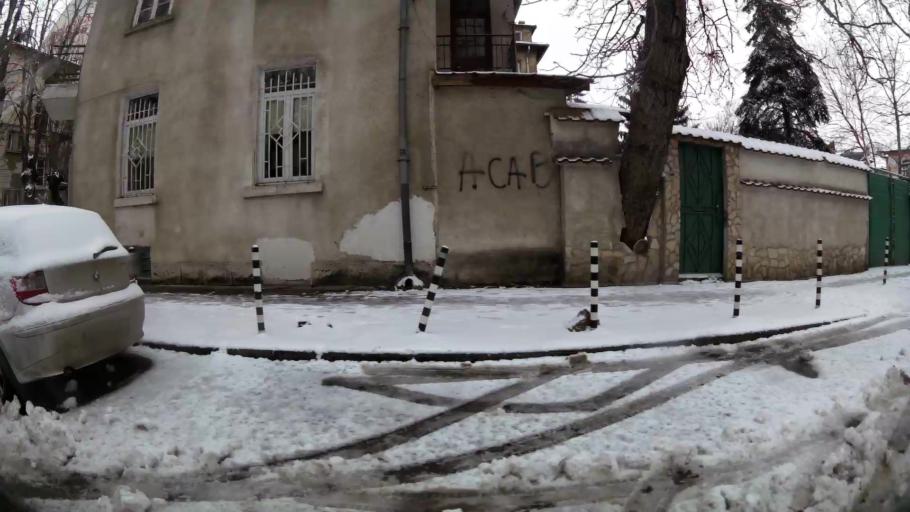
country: BG
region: Sofia-Capital
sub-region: Stolichna Obshtina
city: Sofia
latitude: 42.7060
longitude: 23.3267
